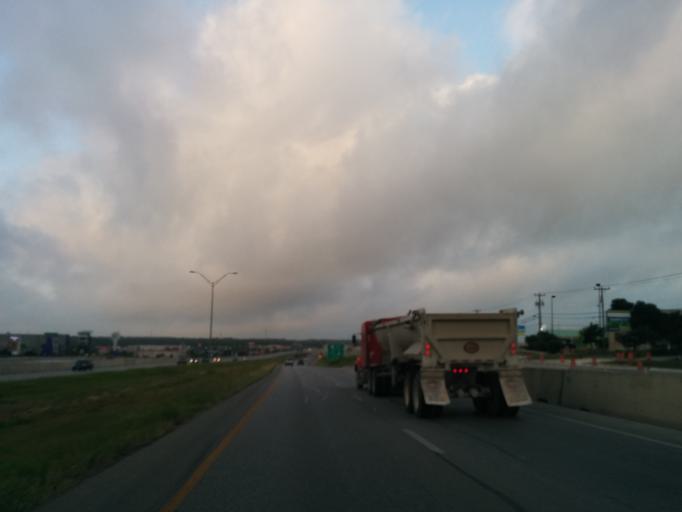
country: US
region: Texas
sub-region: Bexar County
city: Helotes
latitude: 29.5000
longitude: -98.7021
